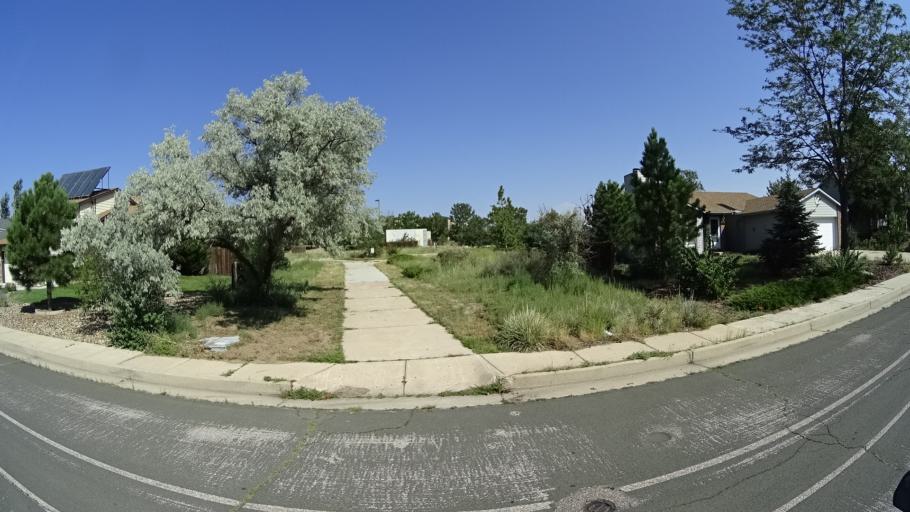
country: US
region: Colorado
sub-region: El Paso County
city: Air Force Academy
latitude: 38.9584
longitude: -104.7828
